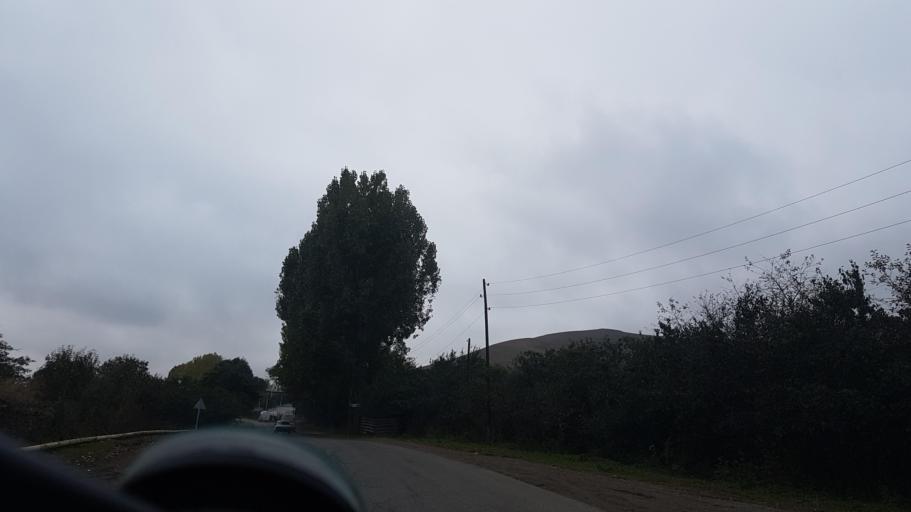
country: AZ
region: Gadabay Rayon
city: Ariqdam
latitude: 40.6563
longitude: 45.8063
